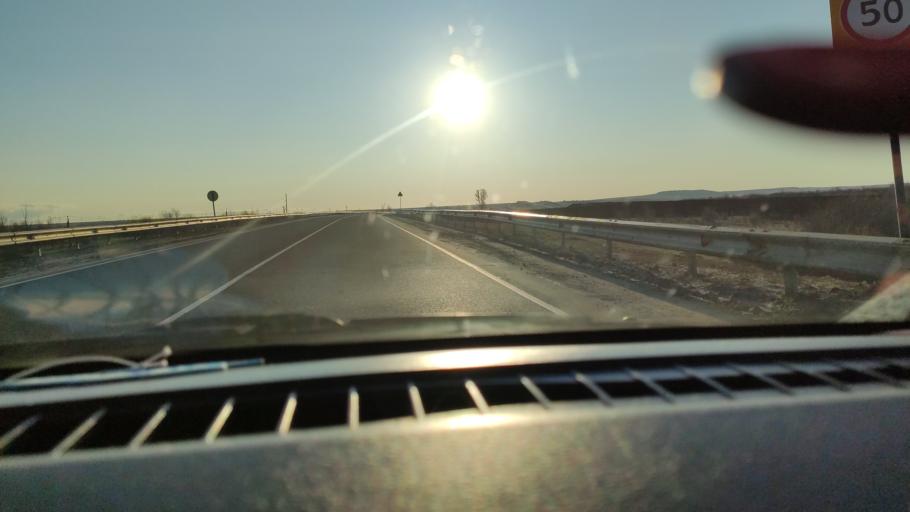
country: RU
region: Saratov
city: Sennoy
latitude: 52.1607
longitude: 47.0467
